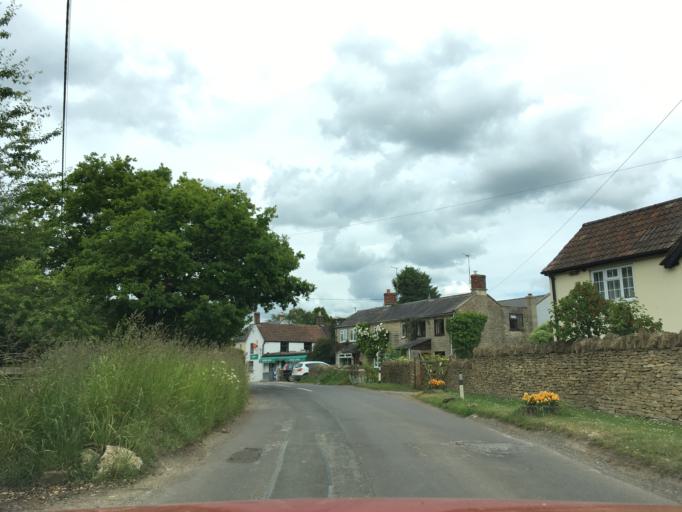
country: GB
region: England
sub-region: Wiltshire
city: Charlton
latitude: 51.5421
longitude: -2.0541
